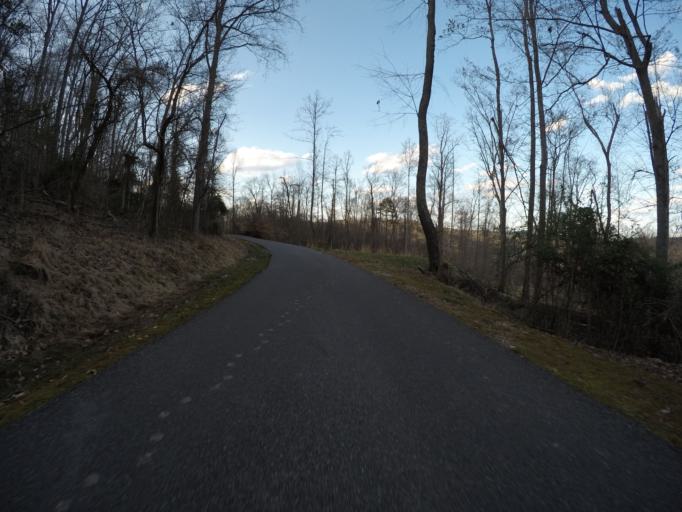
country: US
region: West Virginia
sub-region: Kanawha County
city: Charleston
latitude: 38.3891
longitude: -81.5635
